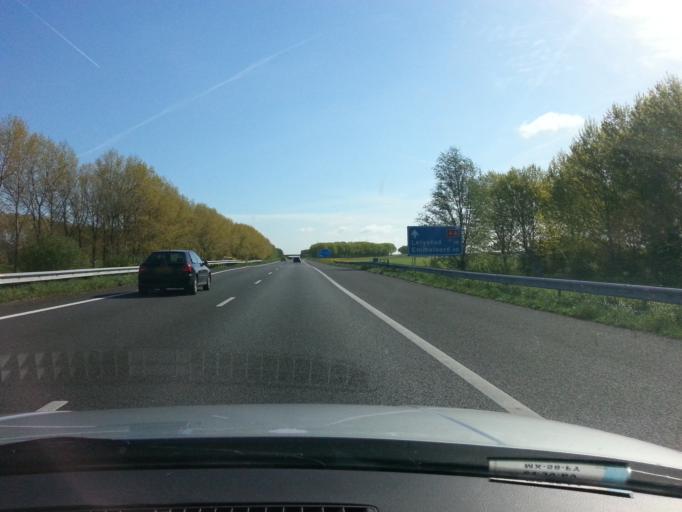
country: NL
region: Flevoland
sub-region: Gemeente Almere
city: Almere Stad
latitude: 52.3920
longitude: 5.3281
